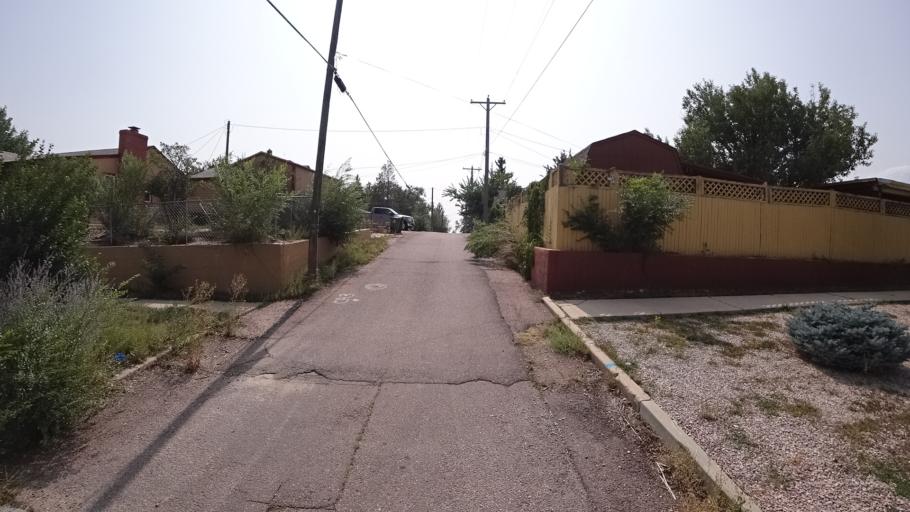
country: US
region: Colorado
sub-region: El Paso County
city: Colorado Springs
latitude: 38.8345
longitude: -104.8000
